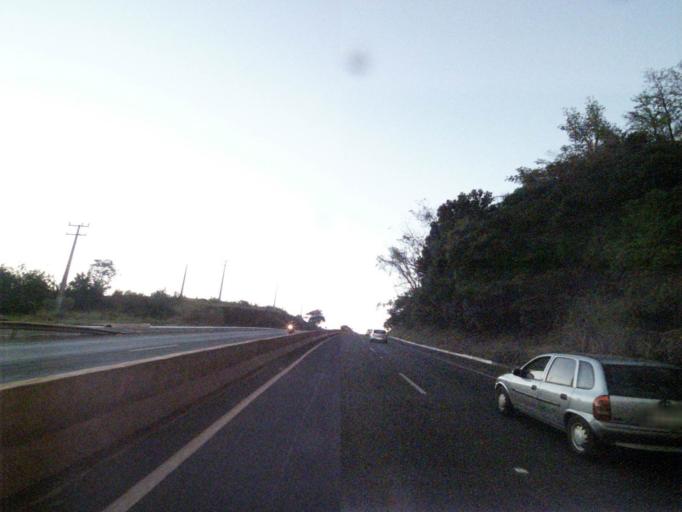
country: BR
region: Parana
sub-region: Londrina
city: Londrina
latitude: -23.3758
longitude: -51.1380
